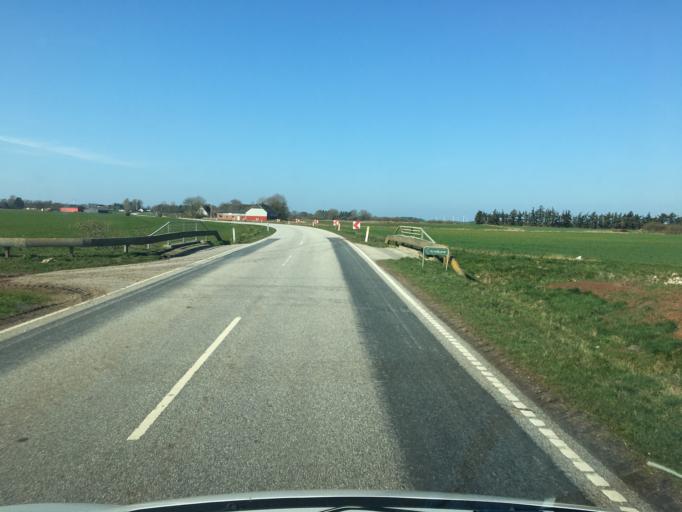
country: DE
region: Schleswig-Holstein
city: Aventoft
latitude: 55.0188
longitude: 8.7416
